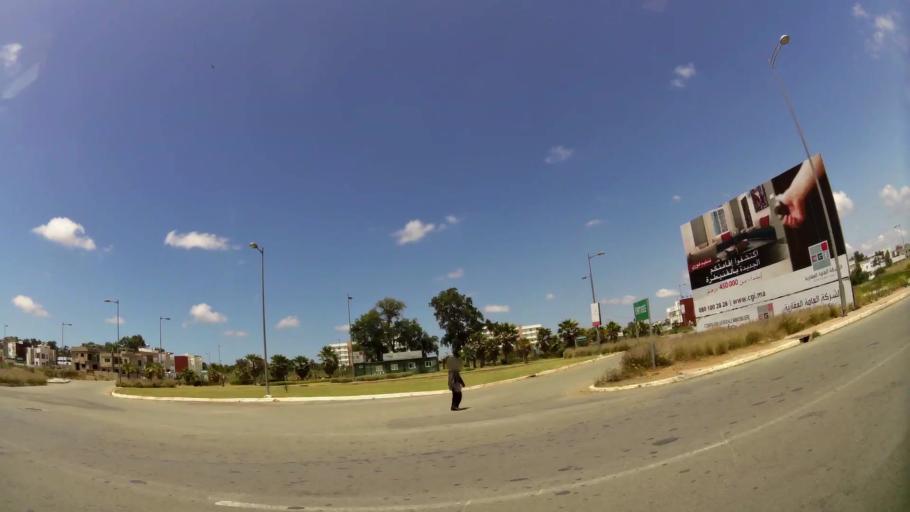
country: MA
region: Gharb-Chrarda-Beni Hssen
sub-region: Kenitra Province
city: Kenitra
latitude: 34.2487
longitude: -6.5623
